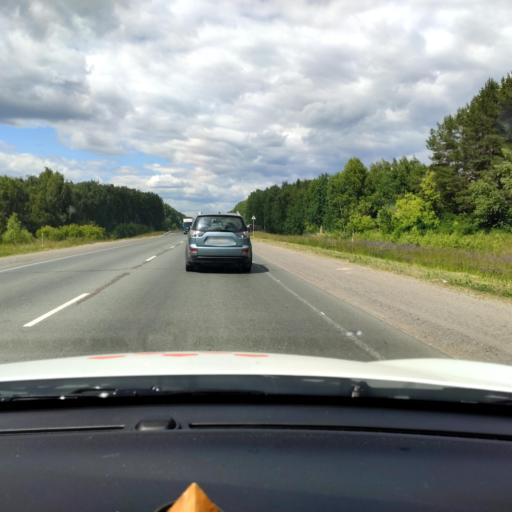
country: RU
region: Mariy-El
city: Pomary
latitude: 55.9351
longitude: 48.3724
